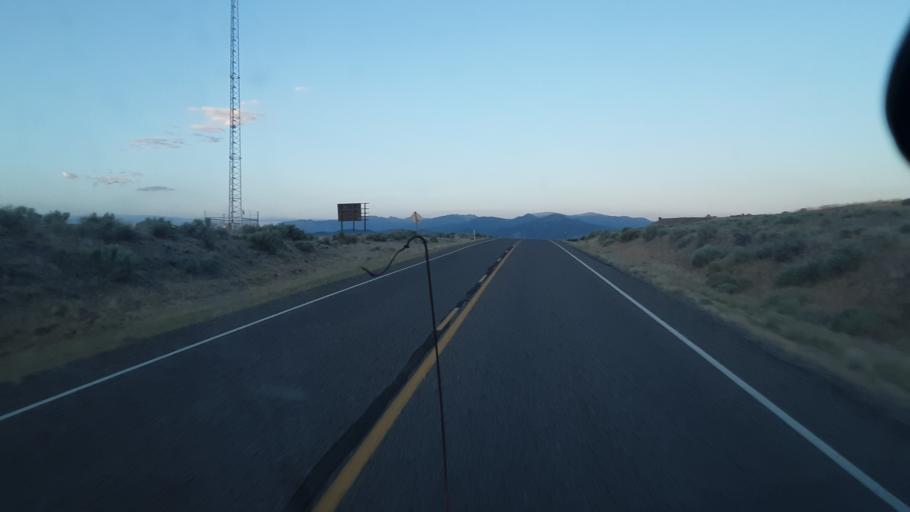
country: US
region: Utah
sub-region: Sevier County
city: Monroe
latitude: 38.6608
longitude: -112.1758
